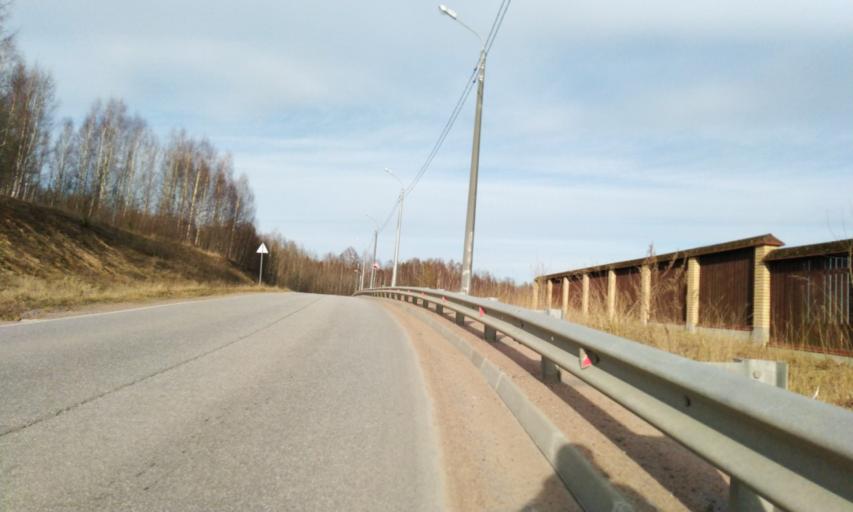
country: RU
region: Leningrad
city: Bugry
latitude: 60.1146
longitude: 30.4255
